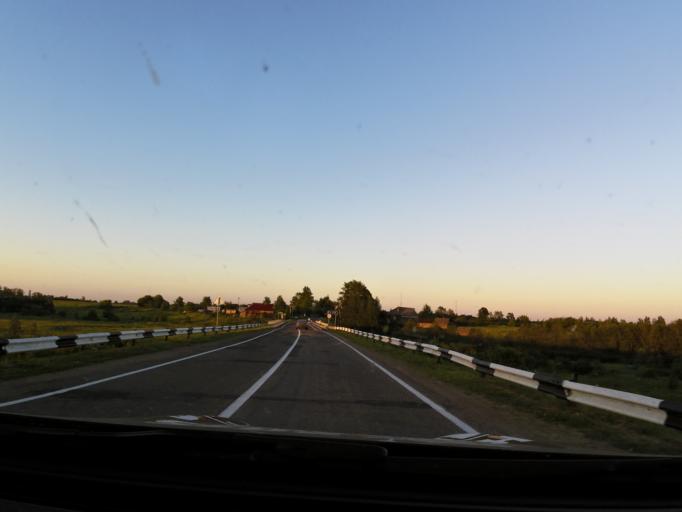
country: RU
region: Jaroslavl
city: Lyubim
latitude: 58.3556
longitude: 40.6587
